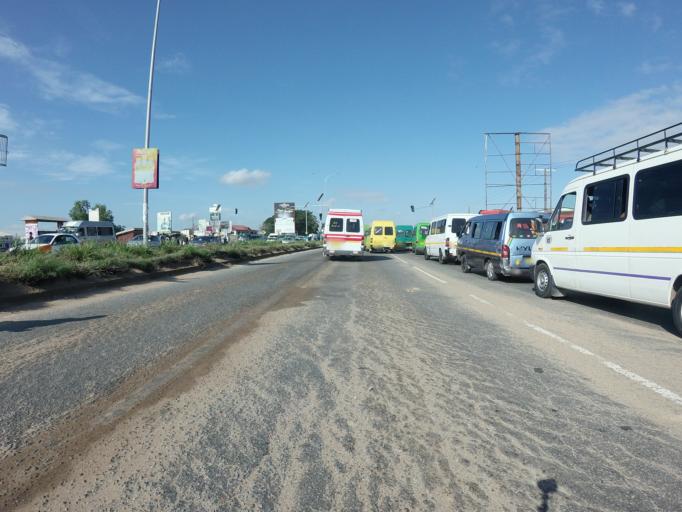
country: GH
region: Greater Accra
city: Gbawe
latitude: 5.5541
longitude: -0.3087
